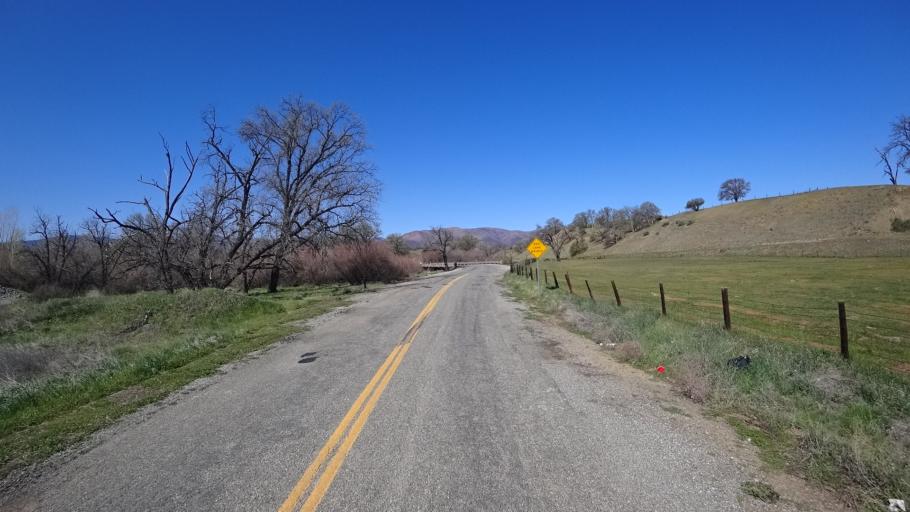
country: US
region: California
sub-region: Glenn County
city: Orland
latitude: 39.6801
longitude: -122.5293
